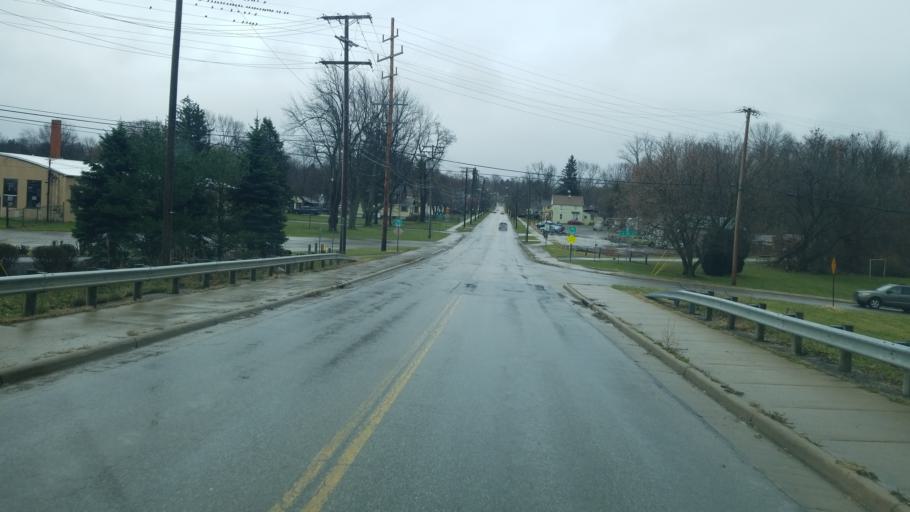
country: US
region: Ohio
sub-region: Ashtabula County
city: Ashtabula
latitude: 41.8587
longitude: -80.7957
